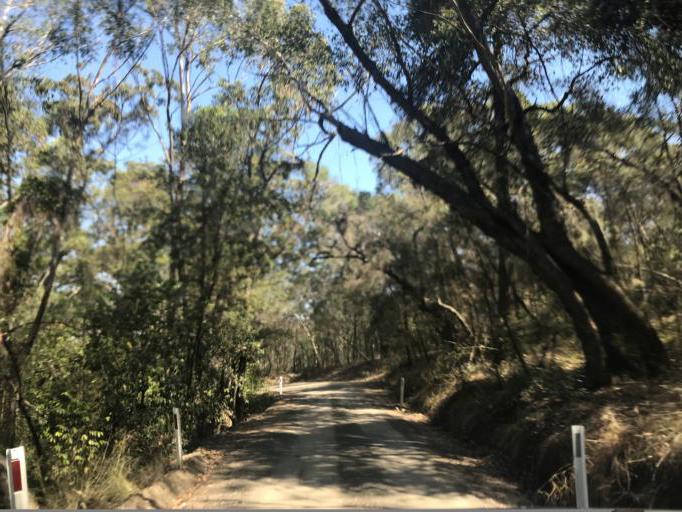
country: AU
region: New South Wales
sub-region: Hawkesbury
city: Pitt Town
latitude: -33.4104
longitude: 150.9226
